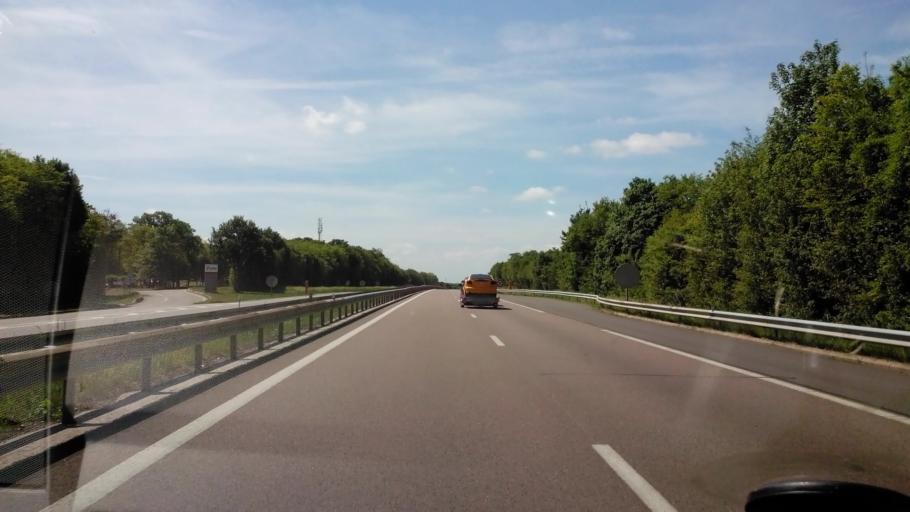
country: FR
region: Lorraine
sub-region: Departement de Meurthe-et-Moselle
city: Colombey-les-Belles
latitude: 48.5094
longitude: 5.9130
